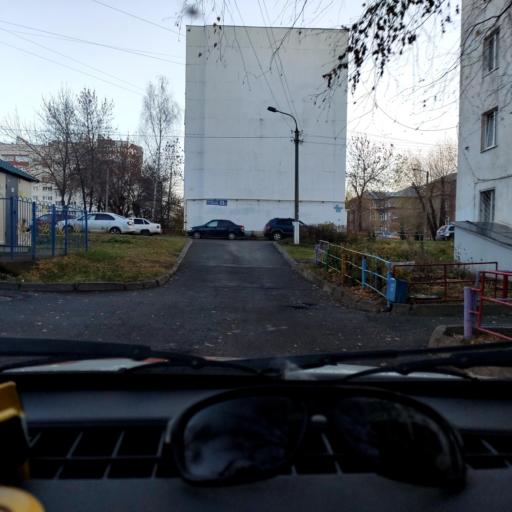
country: RU
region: Bashkortostan
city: Ufa
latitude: 54.7440
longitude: 55.9544
